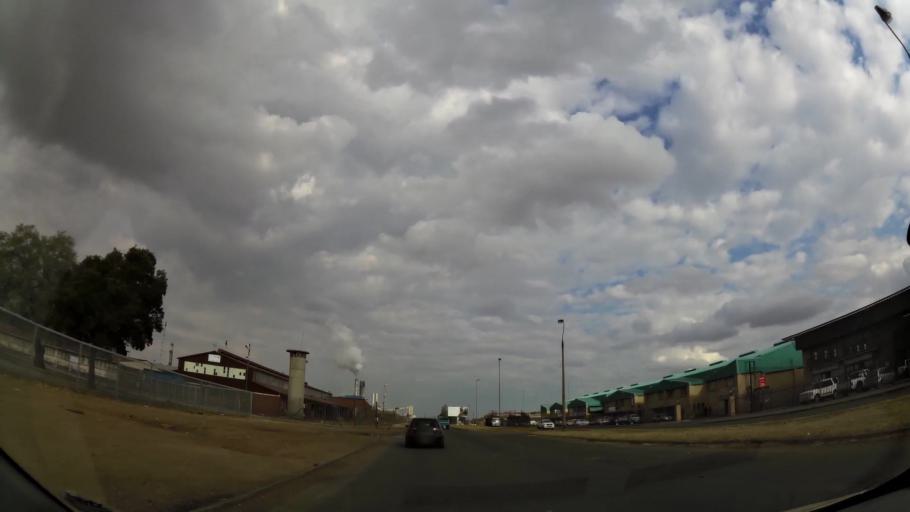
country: ZA
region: Orange Free State
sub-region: Fezile Dabi District Municipality
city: Sasolburg
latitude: -26.8218
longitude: 27.8353
